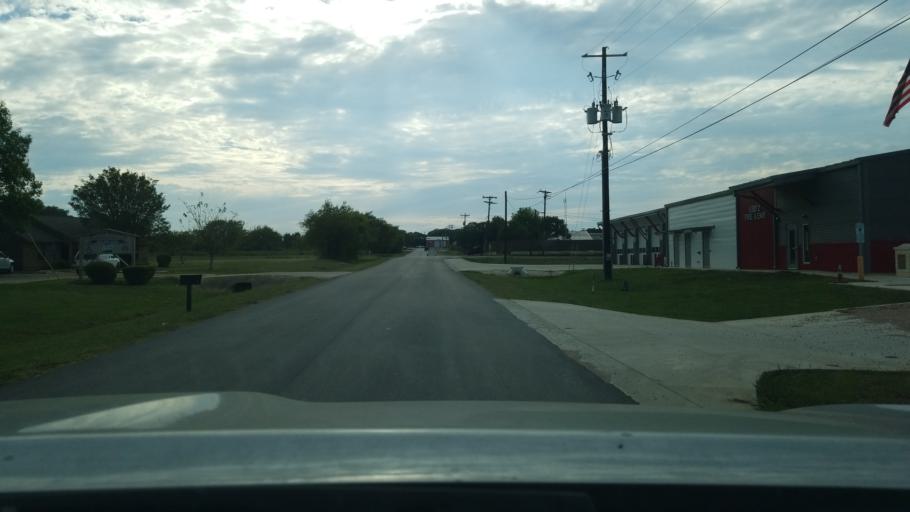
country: US
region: Texas
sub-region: Blanco County
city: Blanco
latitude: 30.0893
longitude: -98.4167
